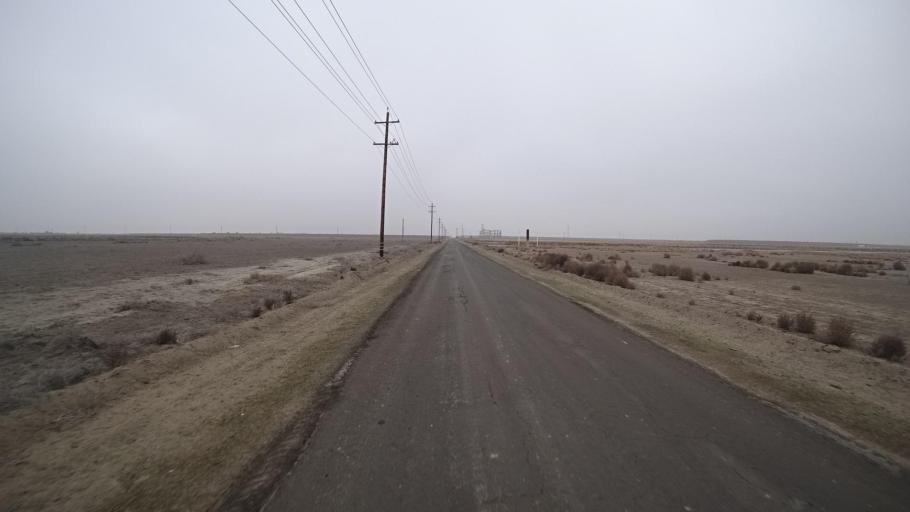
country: US
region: California
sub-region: Kern County
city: Lost Hills
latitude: 35.5966
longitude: -119.5805
